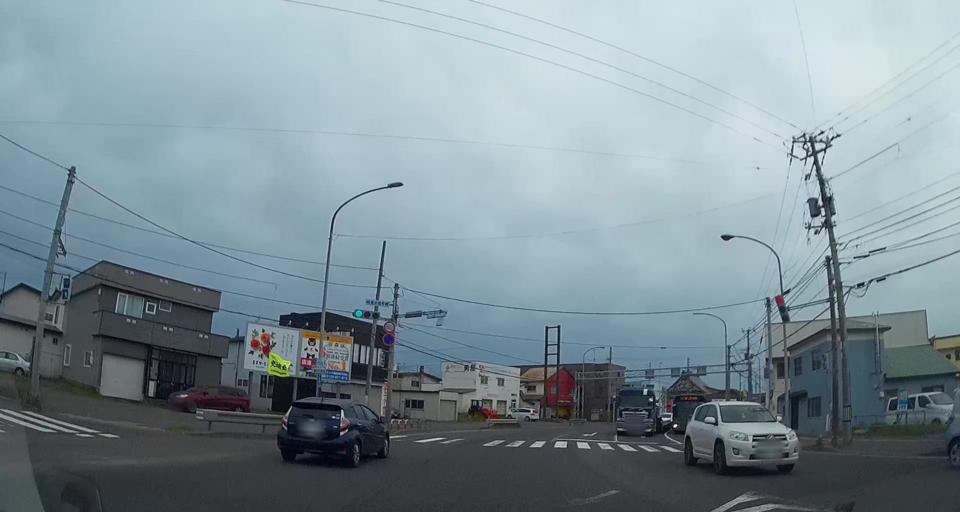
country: JP
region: Hokkaido
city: Tomakomai
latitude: 42.6268
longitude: 141.5925
